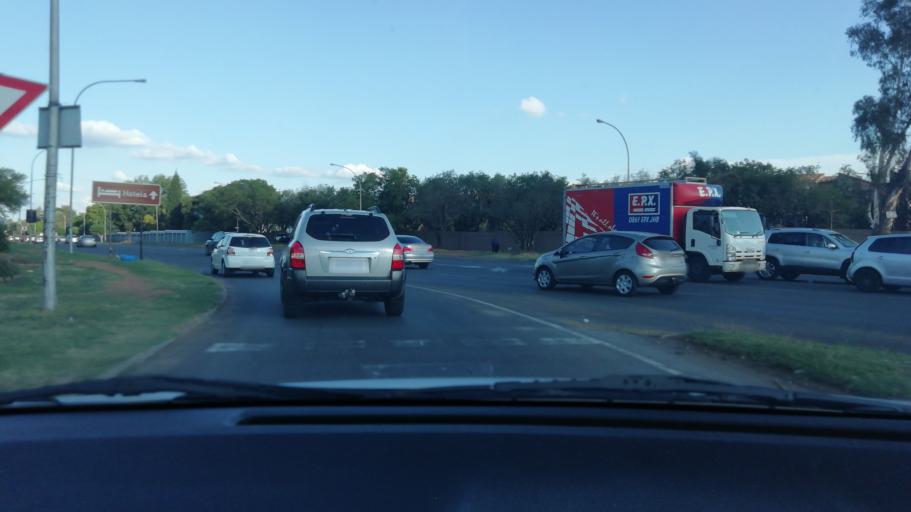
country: ZA
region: Gauteng
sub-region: Ekurhuleni Metropolitan Municipality
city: Boksburg
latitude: -26.1792
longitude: 28.2809
